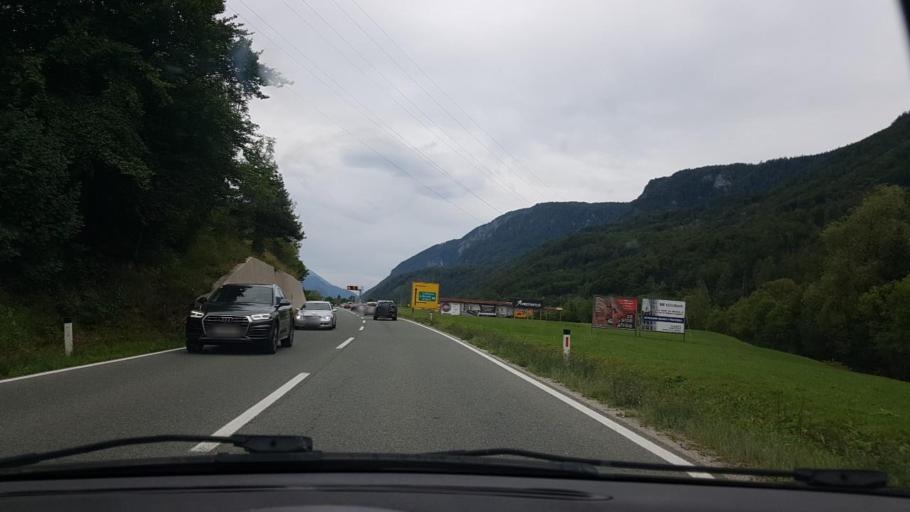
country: SI
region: Jesenice
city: Hrusica
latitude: 46.4499
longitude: 14.0036
